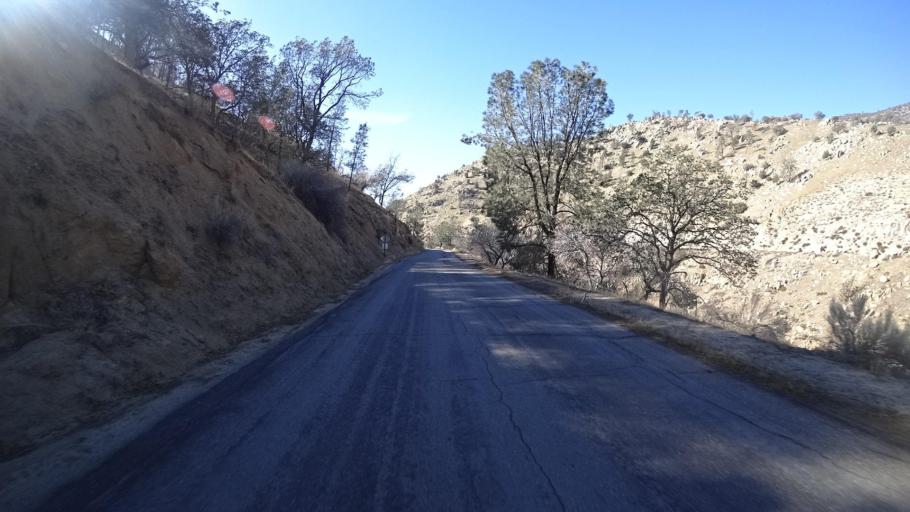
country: US
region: California
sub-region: Kern County
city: Bodfish
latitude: 35.5721
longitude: -118.5640
